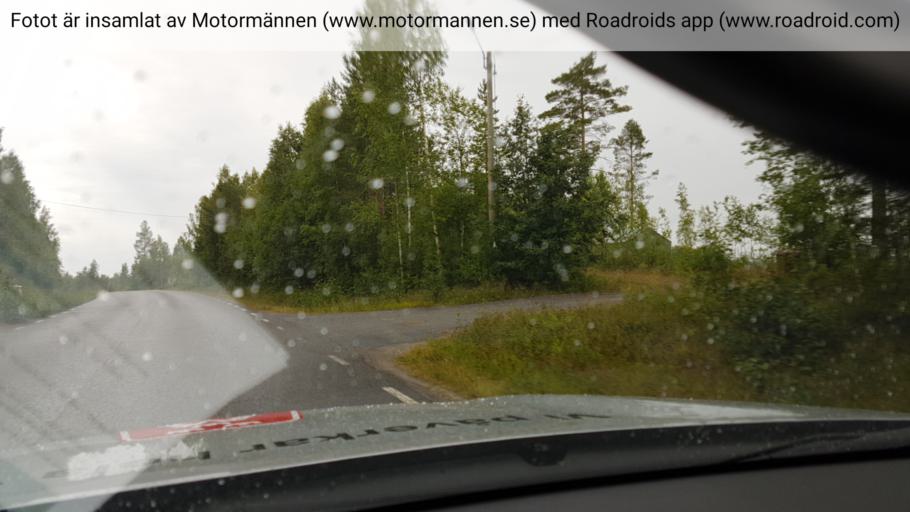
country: SE
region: Norrbotten
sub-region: Bodens Kommun
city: Boden
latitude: 65.8805
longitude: 21.3757
